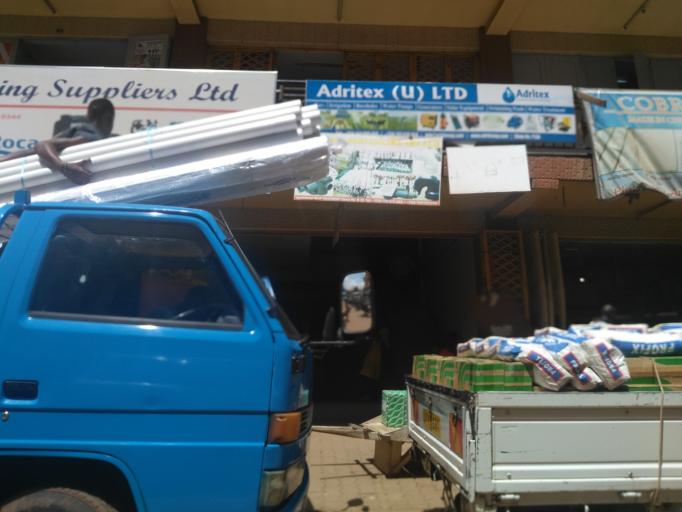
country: UG
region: Central Region
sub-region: Kampala District
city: Kampala
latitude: 0.3108
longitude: 32.5791
